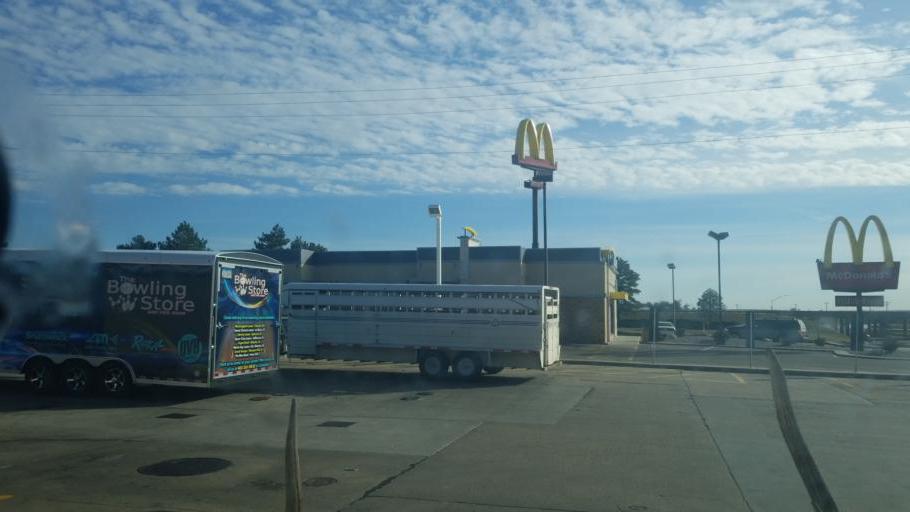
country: US
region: Kansas
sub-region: Russell County
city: Russell
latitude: 38.8658
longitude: -98.8539
